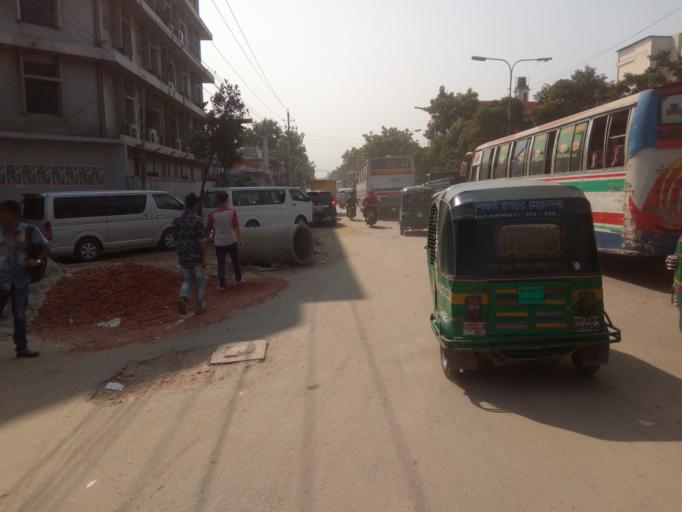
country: BD
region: Dhaka
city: Paltan
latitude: 23.7674
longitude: 90.4008
